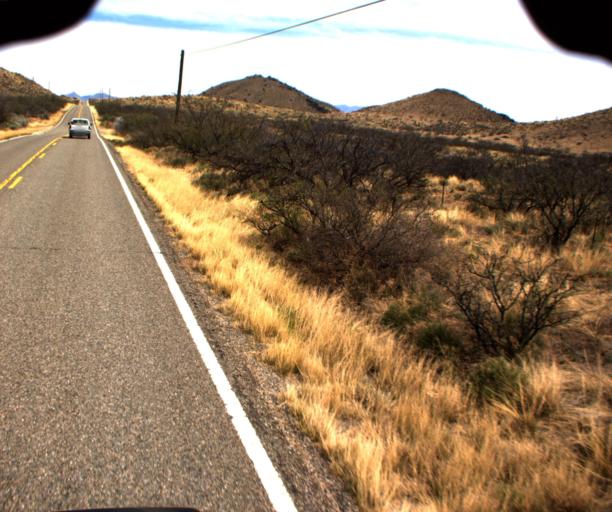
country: US
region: Arizona
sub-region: Cochise County
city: Willcox
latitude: 32.1714
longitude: -109.5985
